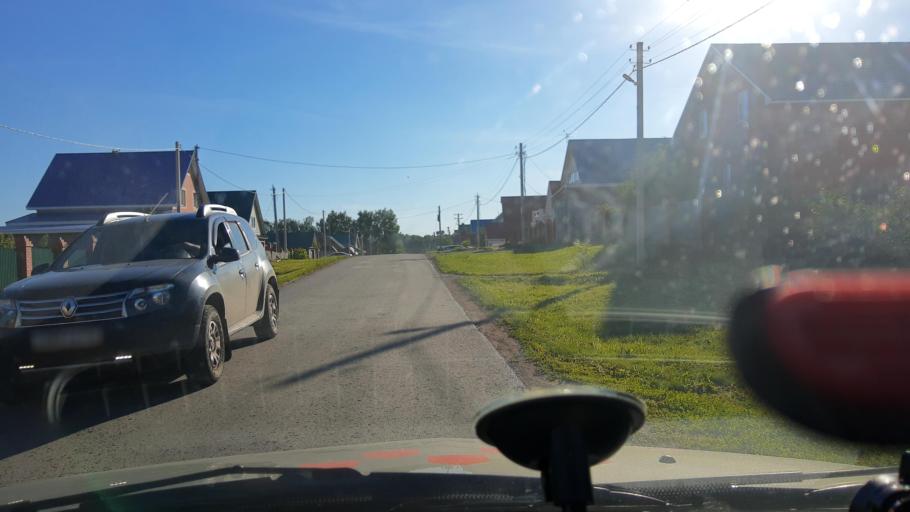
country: RU
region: Bashkortostan
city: Chishmy
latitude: 54.6039
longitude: 55.3811
